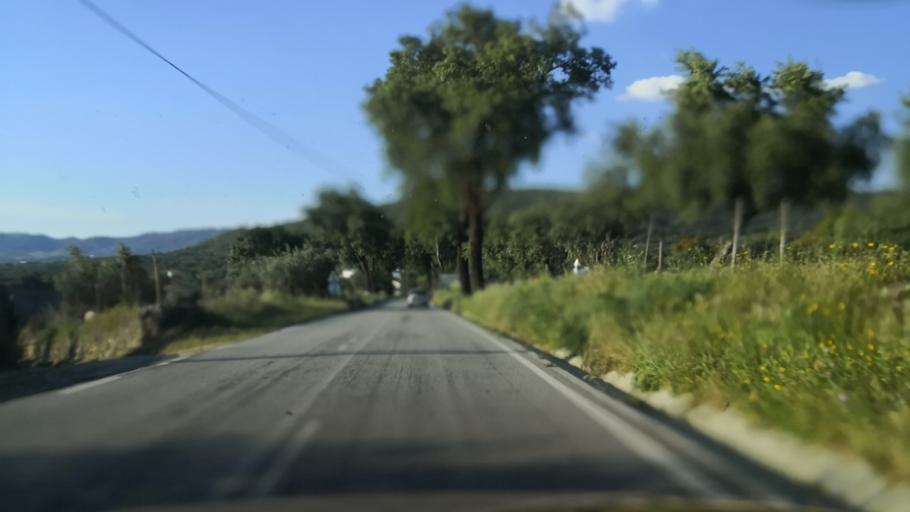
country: PT
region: Portalegre
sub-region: Portalegre
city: Portalegre
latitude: 39.3216
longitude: -7.4372
